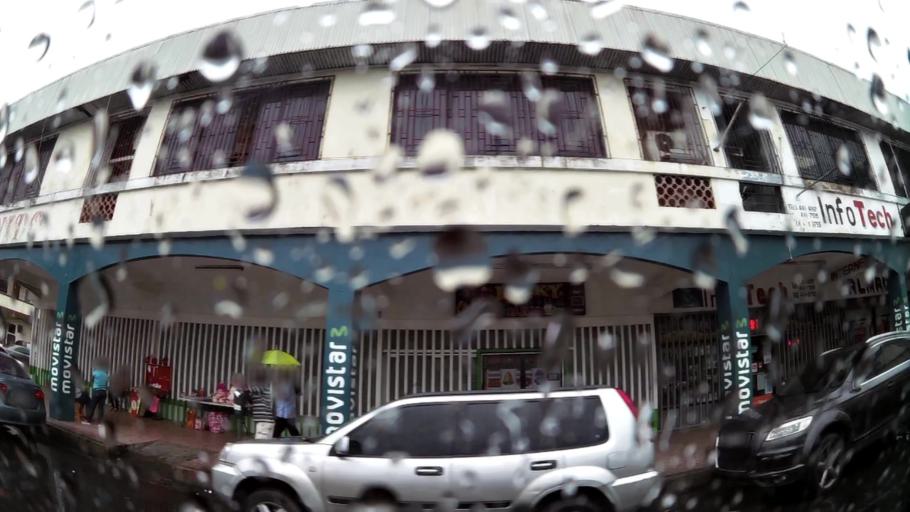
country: PA
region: Colon
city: Colon
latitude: 9.3565
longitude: -79.9026
